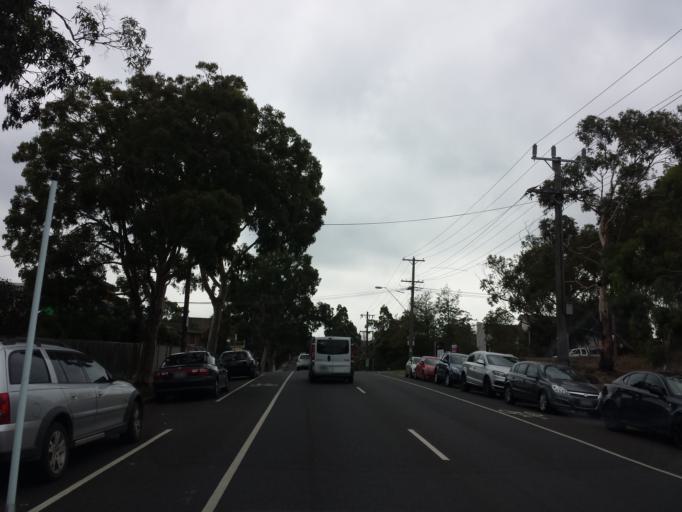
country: AU
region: Victoria
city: Glenferrie
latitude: -37.8399
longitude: 145.0418
